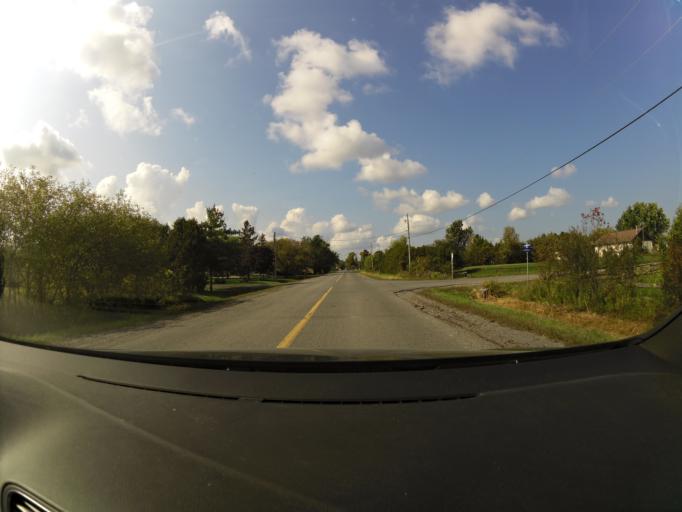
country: CA
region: Ontario
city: Arnprior
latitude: 45.3886
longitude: -76.1847
